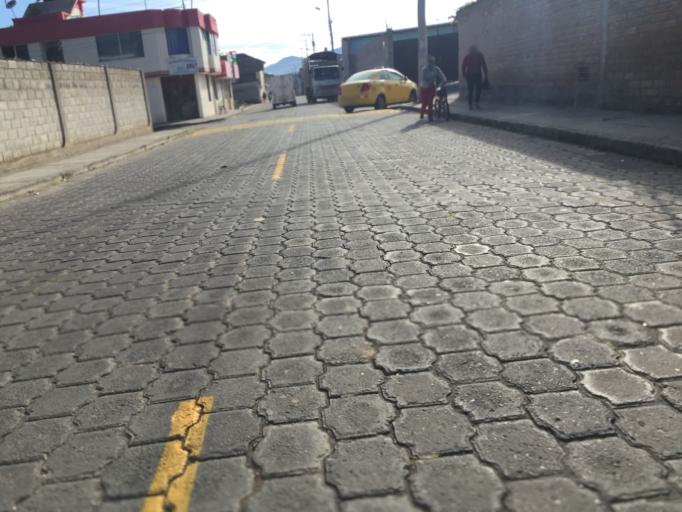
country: EC
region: Imbabura
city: Atuntaqui
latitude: 0.3380
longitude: -78.1951
